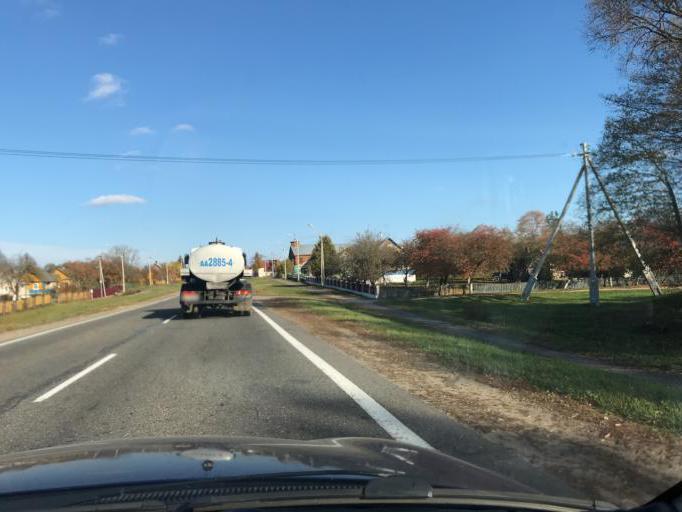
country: BY
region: Grodnenskaya
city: Lida
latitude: 54.0183
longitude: 25.2197
